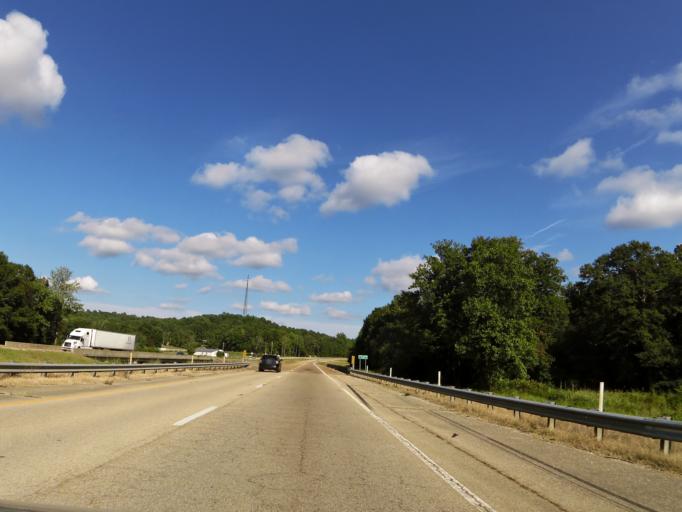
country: US
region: Mississippi
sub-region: Alcorn County
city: Farmington
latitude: 34.8511
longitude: -88.3458
